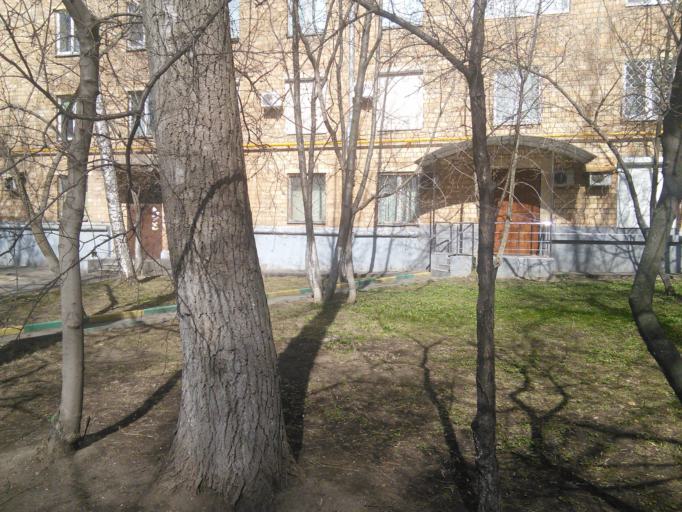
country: RU
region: Moskovskaya
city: Leninskiye Gory
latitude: 55.6988
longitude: 37.5607
